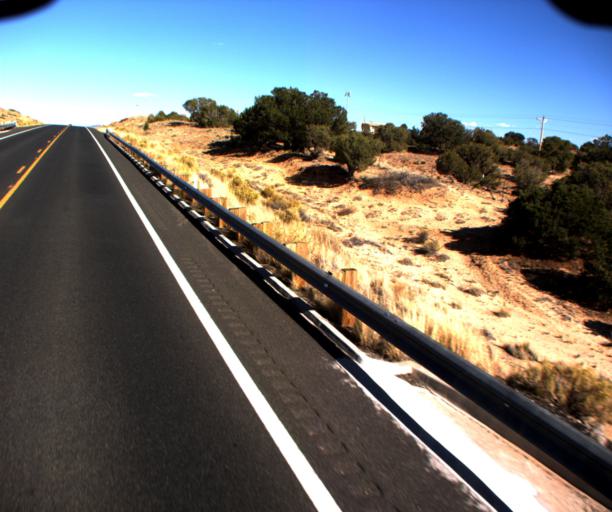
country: US
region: Arizona
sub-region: Coconino County
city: Kaibito
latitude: 36.4455
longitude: -110.7293
